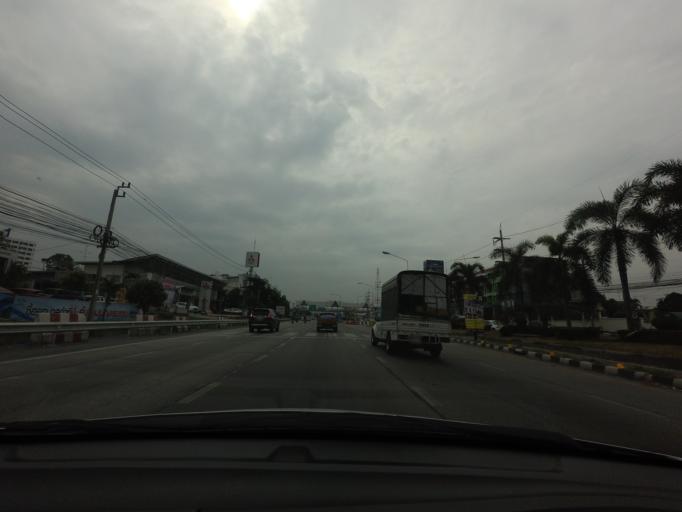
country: TH
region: Samut Prakan
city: Samut Prakan
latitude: 13.6005
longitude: 100.6129
